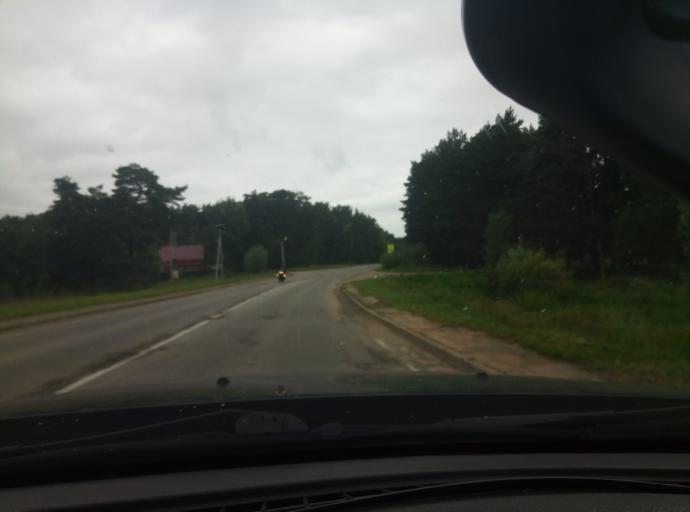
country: RU
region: Kaluga
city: Zhukovo
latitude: 54.9647
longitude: 36.7888
